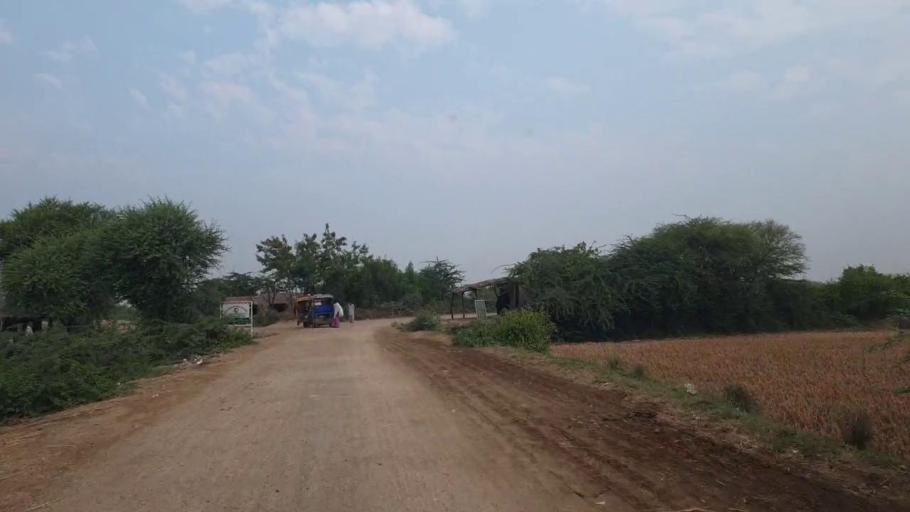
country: PK
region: Sindh
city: Talhar
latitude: 24.8060
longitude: 68.8718
